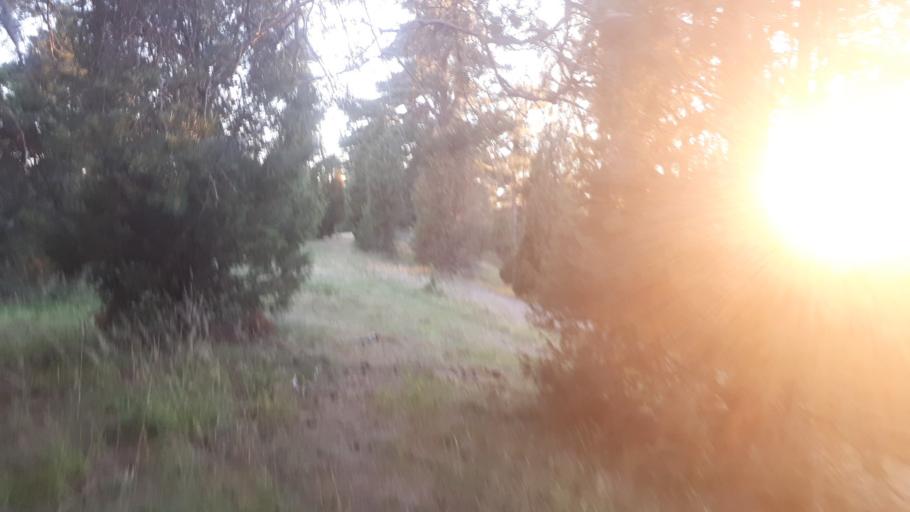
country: SE
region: Soedermanland
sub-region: Flens Kommun
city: Halleforsnas
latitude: 59.0724
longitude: 16.3839
